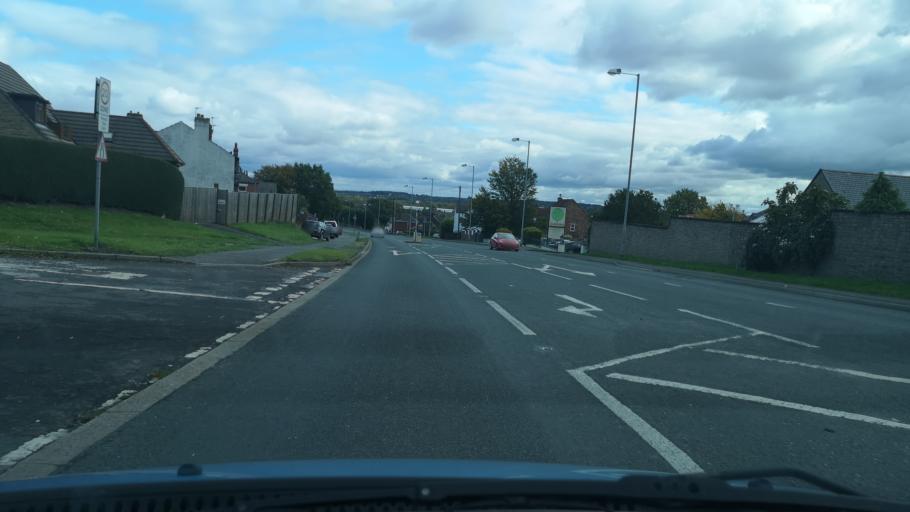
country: GB
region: England
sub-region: City and Borough of Wakefield
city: Horbury
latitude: 53.6569
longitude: -1.5569
